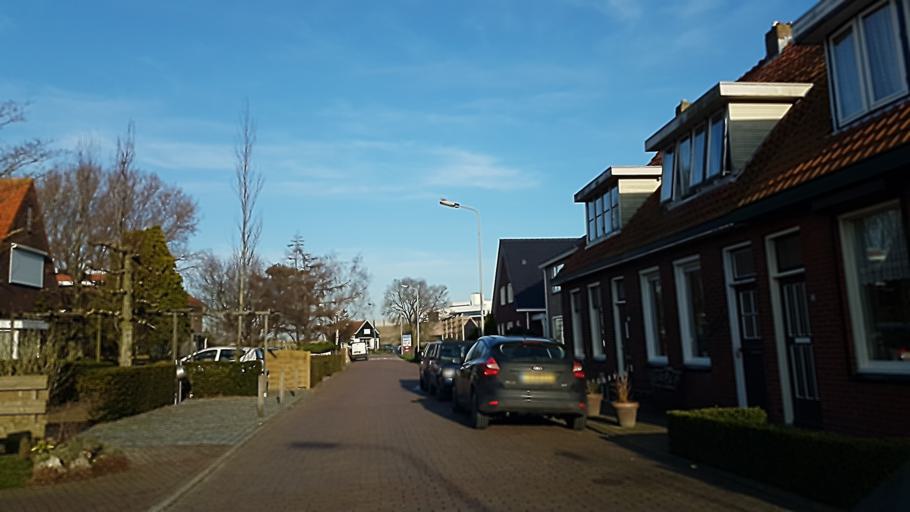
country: NL
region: North Brabant
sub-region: Gemeente Woensdrecht
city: Woensdrecht
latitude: 51.4015
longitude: 4.2105
